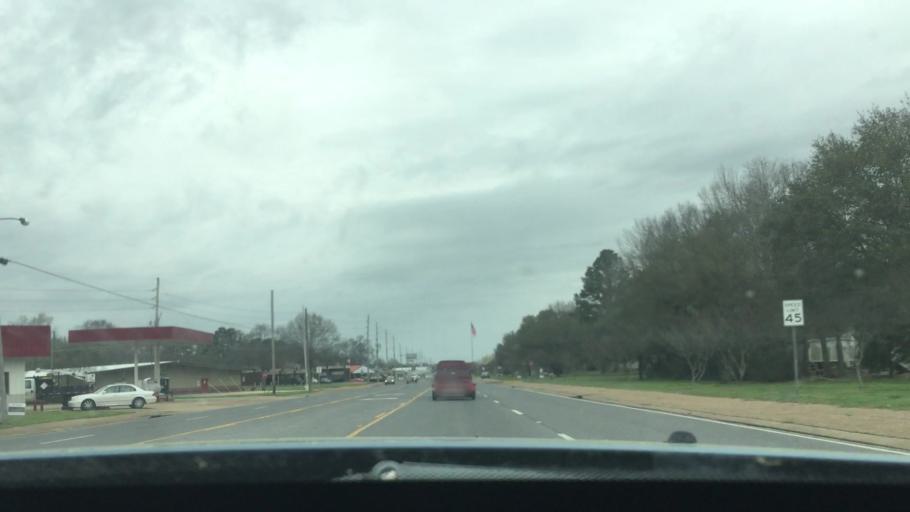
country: US
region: Louisiana
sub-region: Franklin Parish
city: Winnsboro
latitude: 32.1577
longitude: -91.7159
